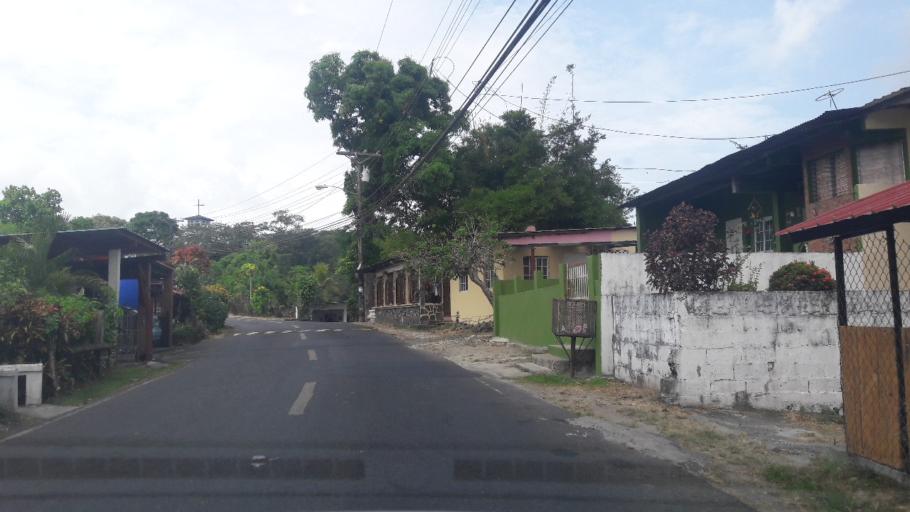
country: PA
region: Panama
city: Alcalde Diaz
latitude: 9.1204
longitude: -79.5564
